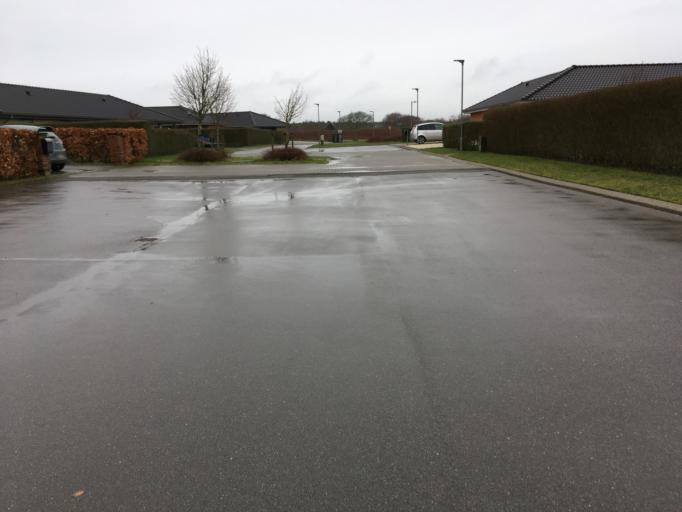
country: DK
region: Central Jutland
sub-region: Ringkobing-Skjern Kommune
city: Ringkobing
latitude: 56.1009
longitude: 8.2681
